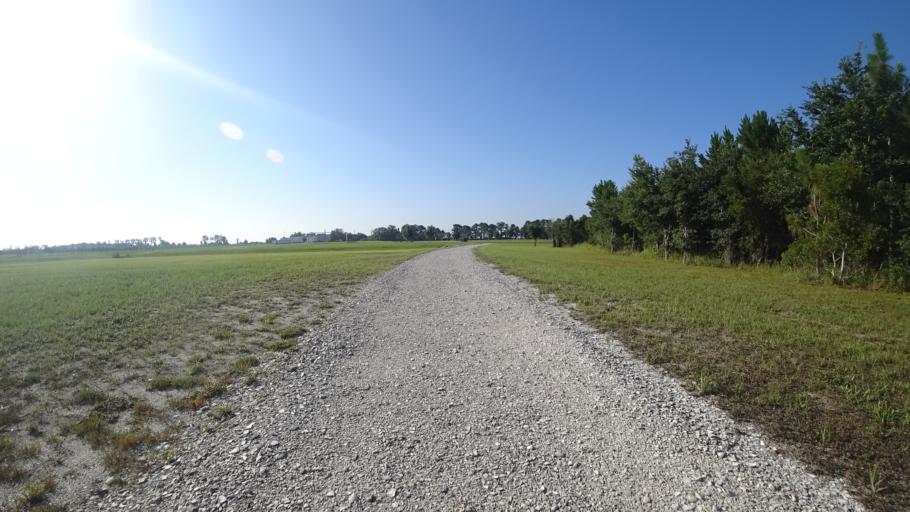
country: US
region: Florida
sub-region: Hillsborough County
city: Wimauma
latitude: 27.5867
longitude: -82.1772
